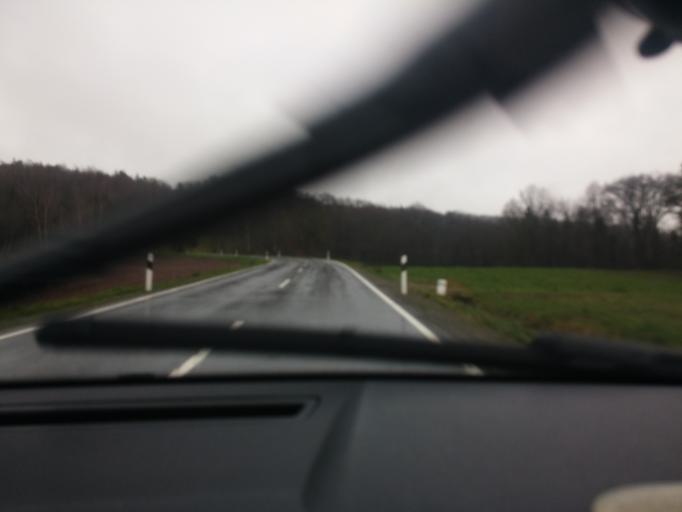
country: DE
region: Hesse
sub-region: Regierungsbezirk Darmstadt
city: Brensbach
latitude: 49.7587
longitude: 8.9023
